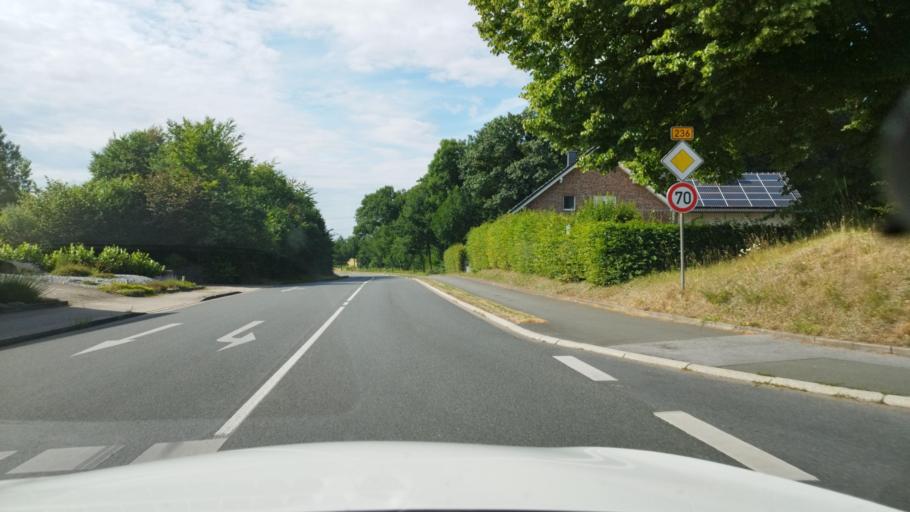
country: DE
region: North Rhine-Westphalia
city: Lunen
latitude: 51.6559
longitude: 7.5017
